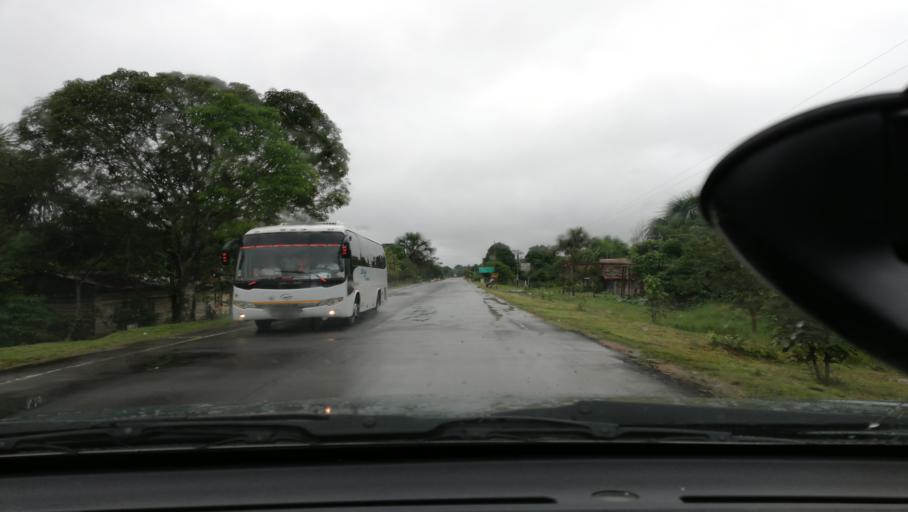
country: PE
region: Loreto
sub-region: Provincia de Maynas
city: San Juan
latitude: -4.1014
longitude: -73.4554
